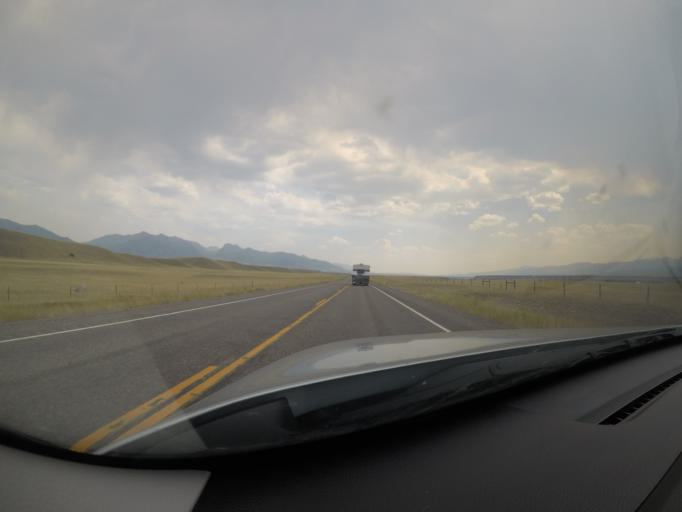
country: US
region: Montana
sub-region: Madison County
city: Virginia City
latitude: 45.1273
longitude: -111.6664
